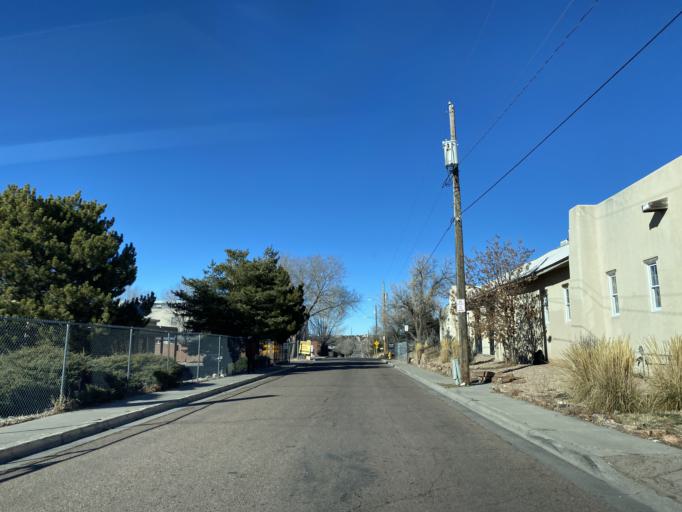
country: US
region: New Mexico
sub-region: Santa Fe County
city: Agua Fria
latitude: 35.6587
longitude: -105.9876
